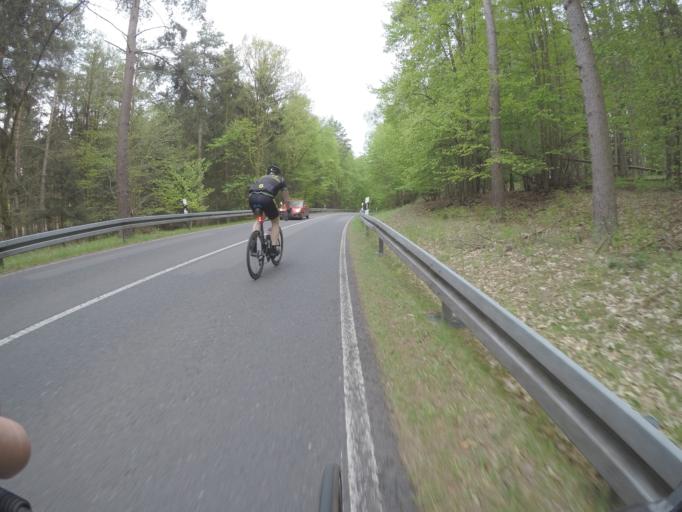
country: DE
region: Brandenburg
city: Joachimsthal
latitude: 52.9461
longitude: 13.7490
